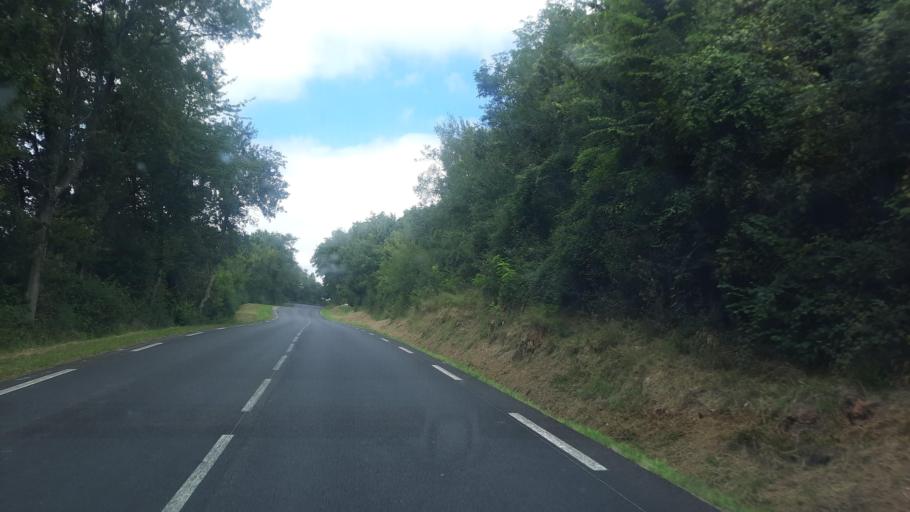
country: FR
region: Midi-Pyrenees
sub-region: Departement des Hautes-Pyrenees
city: Orleix
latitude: 43.2788
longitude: 0.1903
